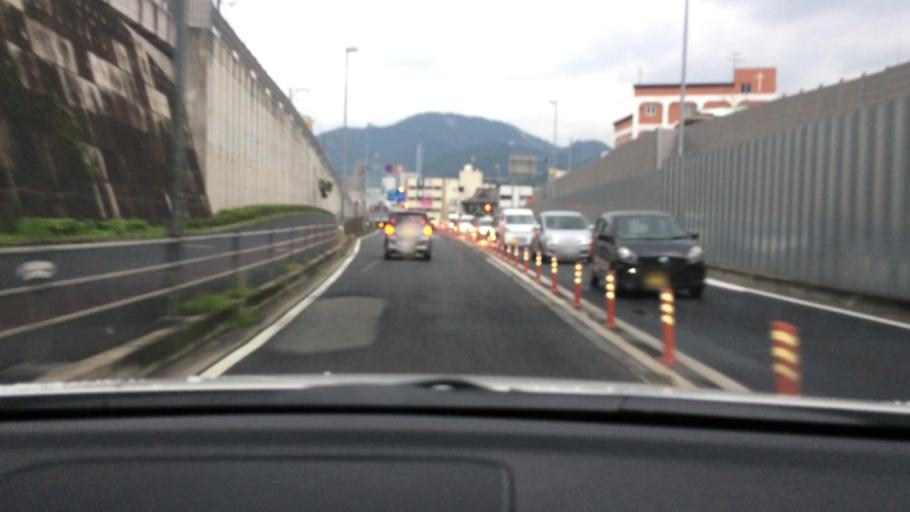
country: JP
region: Hiroshima
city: Kure
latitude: 34.2491
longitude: 132.5769
